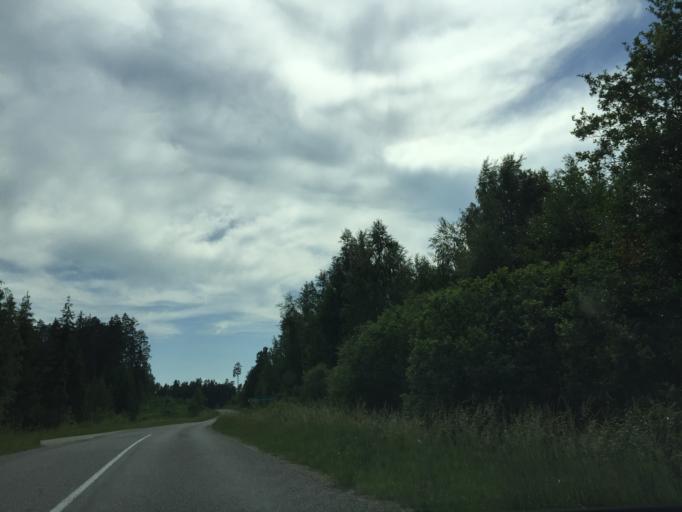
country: LV
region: Tukuma Rajons
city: Tukums
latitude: 57.0220
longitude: 23.2484
